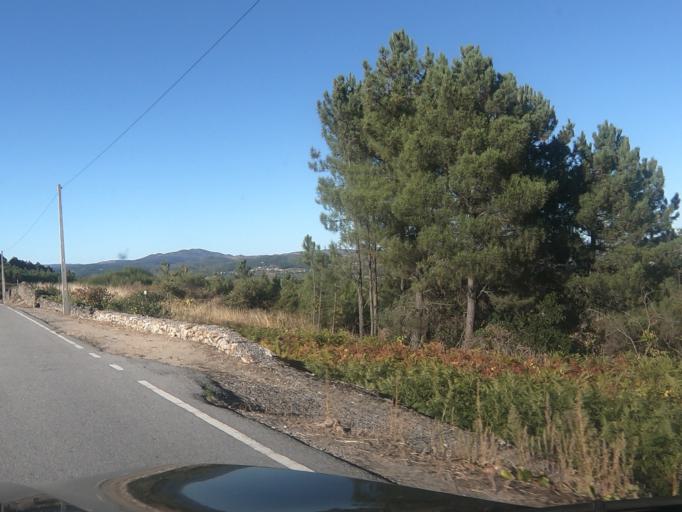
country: PT
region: Vila Real
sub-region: Sabrosa
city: Sabrosa
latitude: 41.2829
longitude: -7.5762
